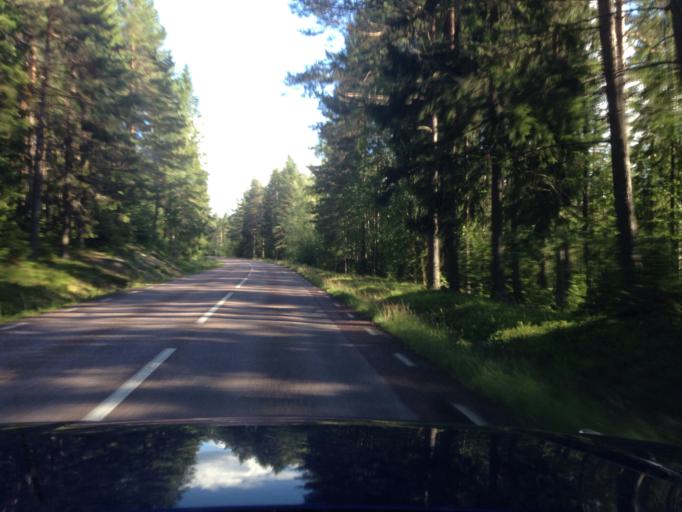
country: SE
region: Dalarna
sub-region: Ludvika Kommun
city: Grangesberg
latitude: 60.1359
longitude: 15.0034
